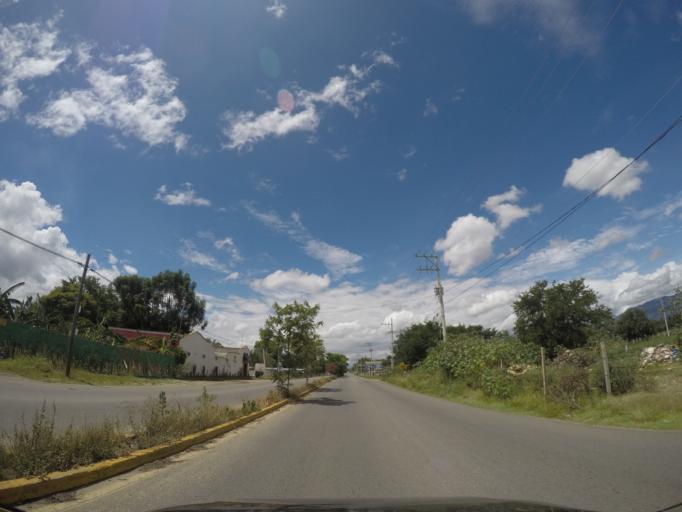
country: MX
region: Oaxaca
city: San Raymundo Jalpam
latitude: 16.9742
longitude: -96.7502
